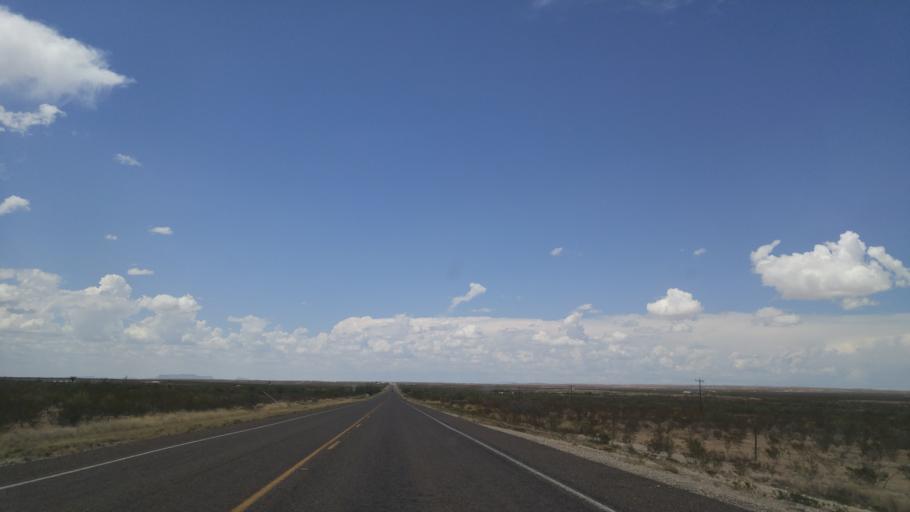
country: US
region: Texas
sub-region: Brewster County
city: Alpine
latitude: 29.6002
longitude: -103.5605
